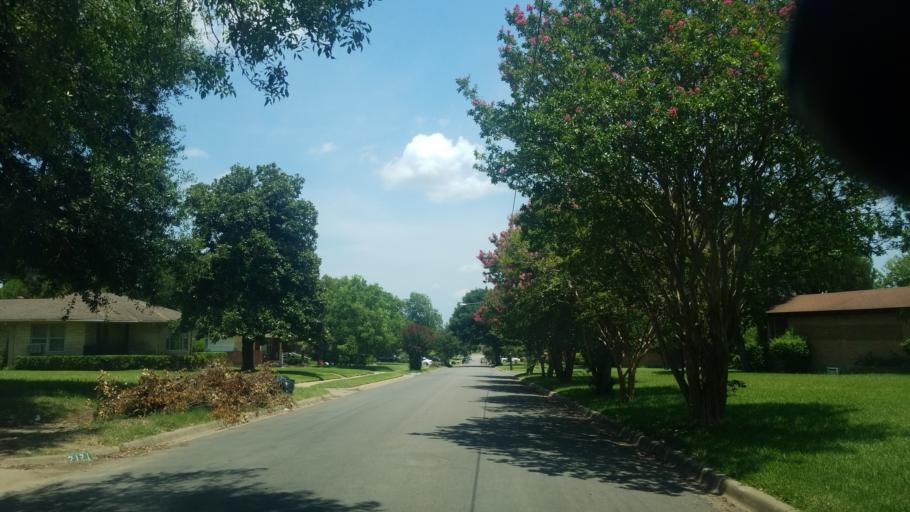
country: US
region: Texas
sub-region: Dallas County
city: Dallas
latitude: 32.7199
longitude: -96.7899
